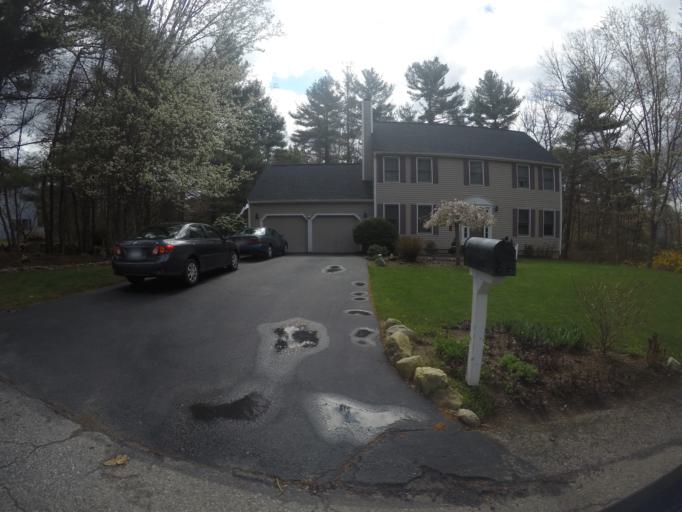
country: US
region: Massachusetts
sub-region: Bristol County
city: Easton
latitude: 42.0418
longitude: -71.1299
